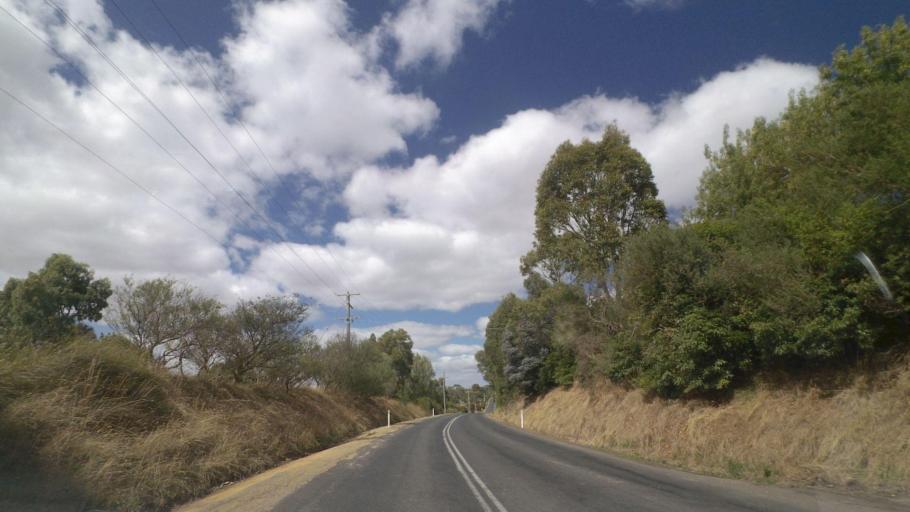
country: AU
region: Victoria
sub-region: Cardinia
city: Koo-Wee-Rup
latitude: -38.3222
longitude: 145.6717
